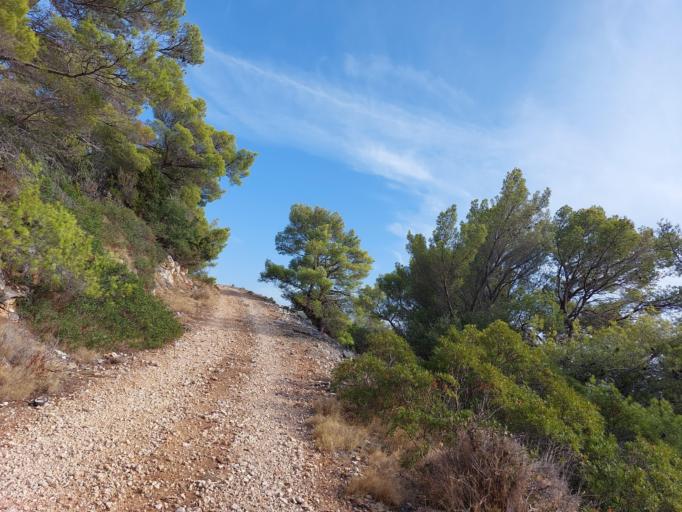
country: HR
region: Dubrovacko-Neretvanska
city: Smokvica
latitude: 42.7332
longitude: 16.8295
